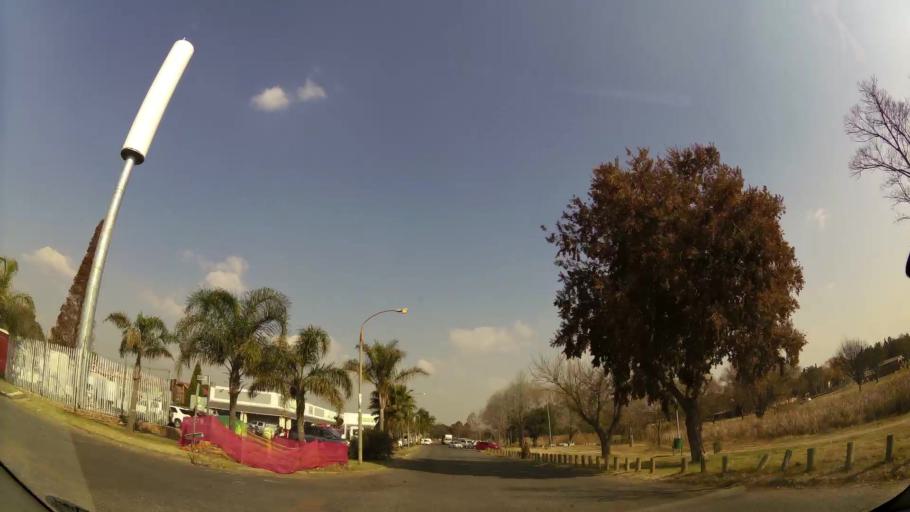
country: ZA
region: Gauteng
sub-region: Ekurhuleni Metropolitan Municipality
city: Benoni
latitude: -26.1533
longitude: 28.2889
